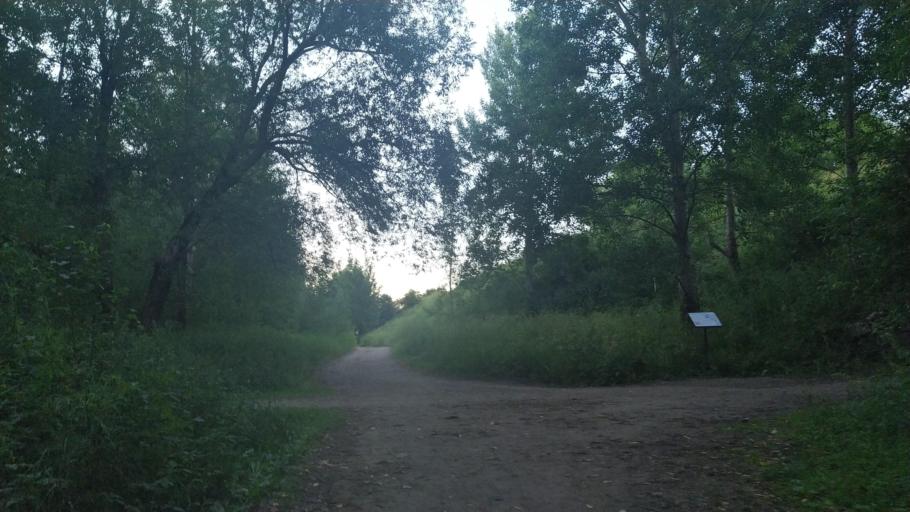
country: RU
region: St.-Petersburg
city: Kronshtadt
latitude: 60.0249
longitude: 29.6729
